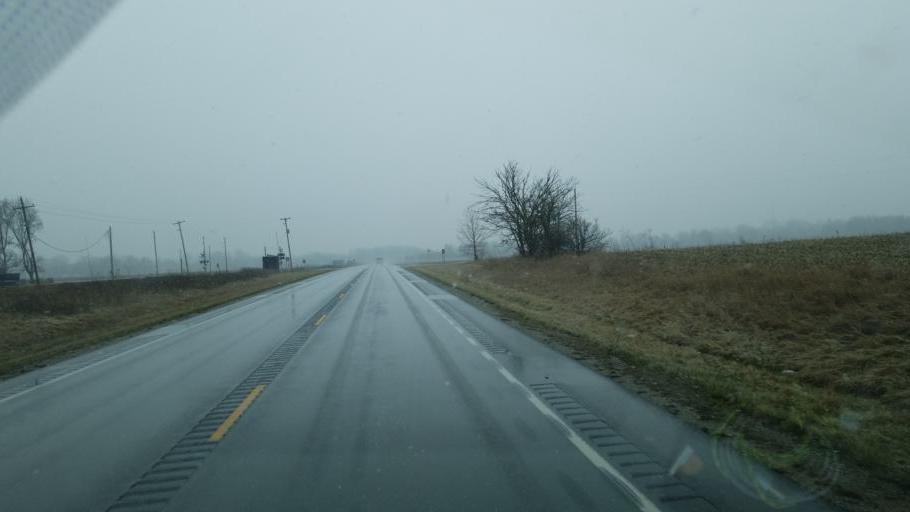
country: US
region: Indiana
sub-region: Wabash County
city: Mount Vernon
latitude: 40.6822
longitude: -85.7342
